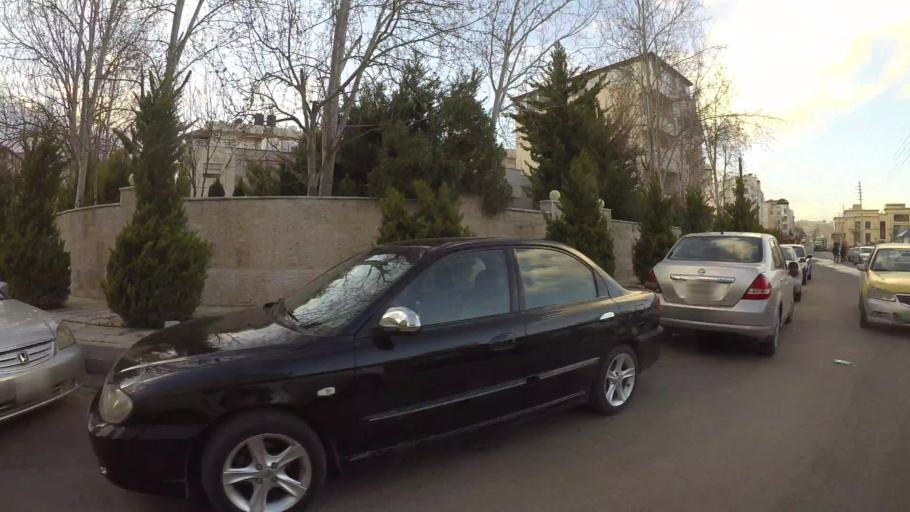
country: JO
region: Amman
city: Al Jubayhah
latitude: 31.9826
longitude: 35.8641
